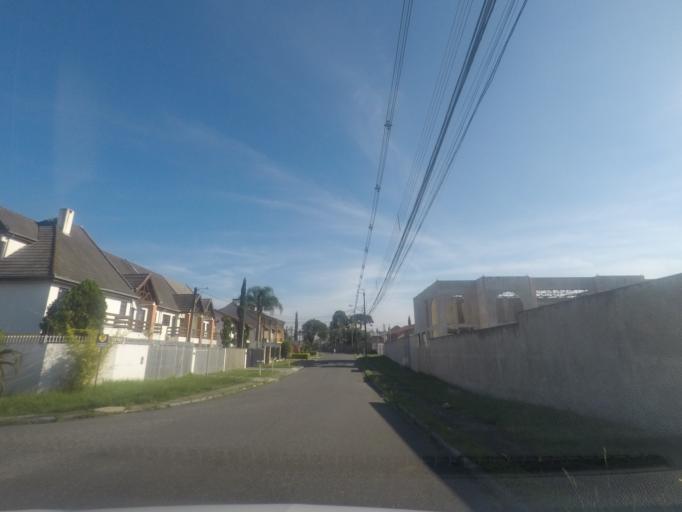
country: BR
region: Parana
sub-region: Pinhais
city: Pinhais
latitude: -25.4728
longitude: -49.2193
